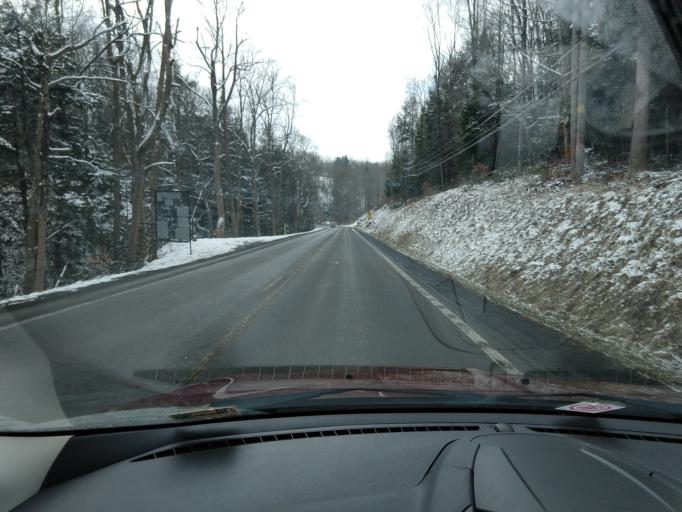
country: US
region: West Virginia
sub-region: Nicholas County
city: Craigsville
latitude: 38.3111
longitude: -80.6569
